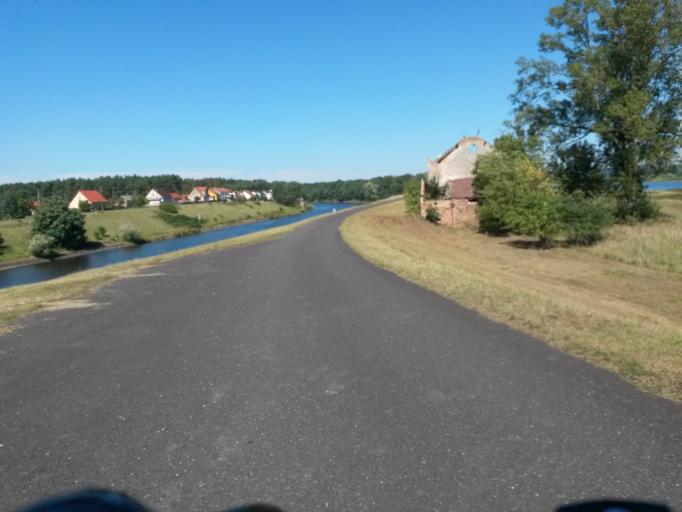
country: PL
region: West Pomeranian Voivodeship
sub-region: Powiat gryfinski
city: Cedynia
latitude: 52.8821
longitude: 14.1561
